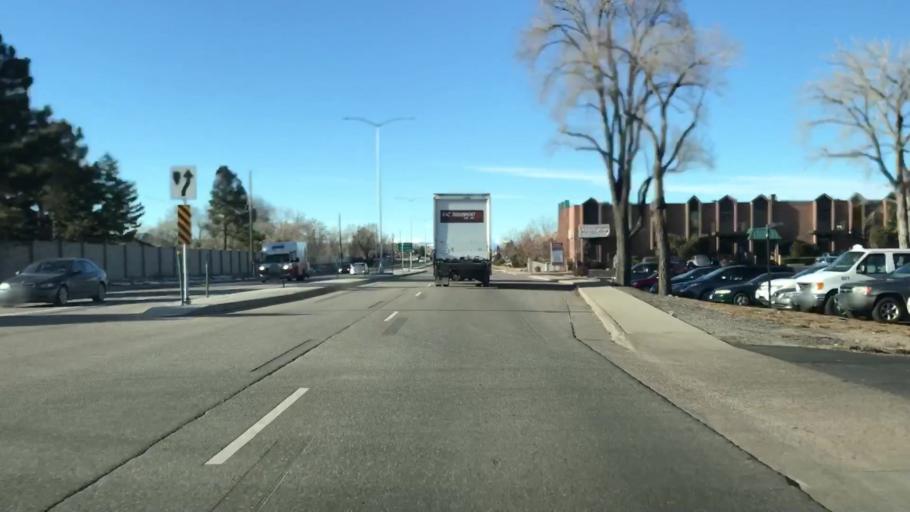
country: US
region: Colorado
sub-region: Arapahoe County
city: Glendale
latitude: 39.6874
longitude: -104.8868
